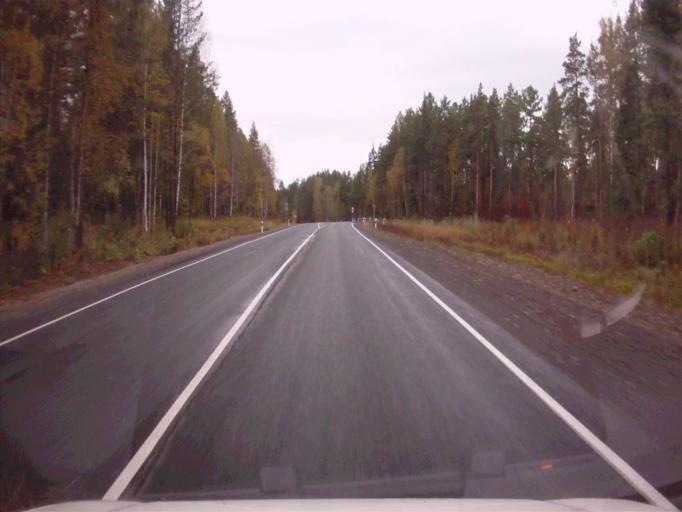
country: RU
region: Chelyabinsk
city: Nyazepetrovsk
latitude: 56.0602
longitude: 59.7307
